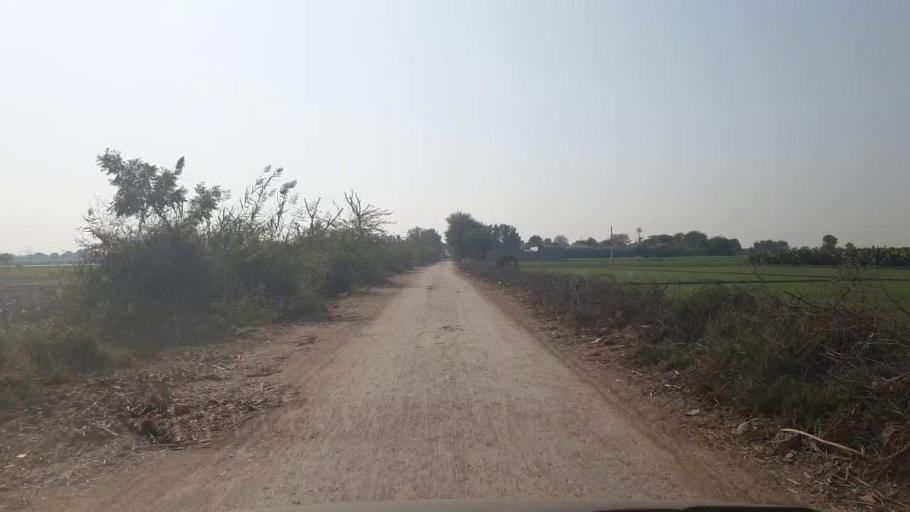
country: PK
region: Sindh
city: Tando Adam
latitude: 25.7544
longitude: 68.6154
